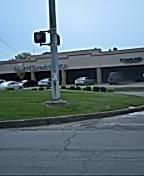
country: US
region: Kentucky
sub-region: Jefferson County
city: Hurstbourne
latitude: 38.2461
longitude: -85.5732
